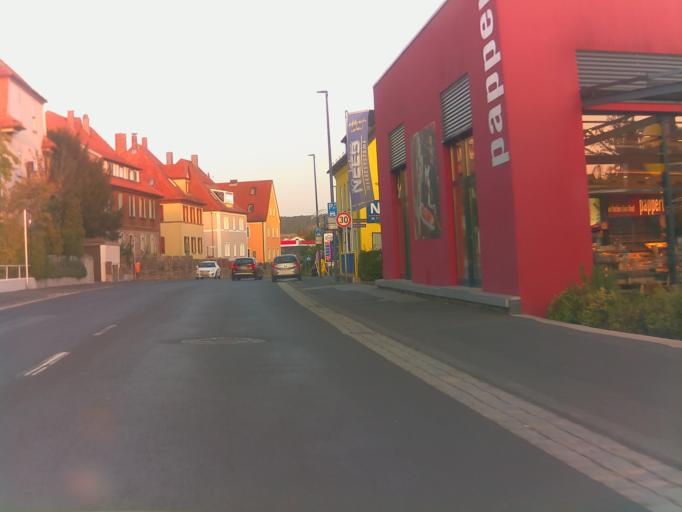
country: DE
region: Bavaria
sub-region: Regierungsbezirk Unterfranken
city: Hammelburg
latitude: 50.1154
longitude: 9.8952
